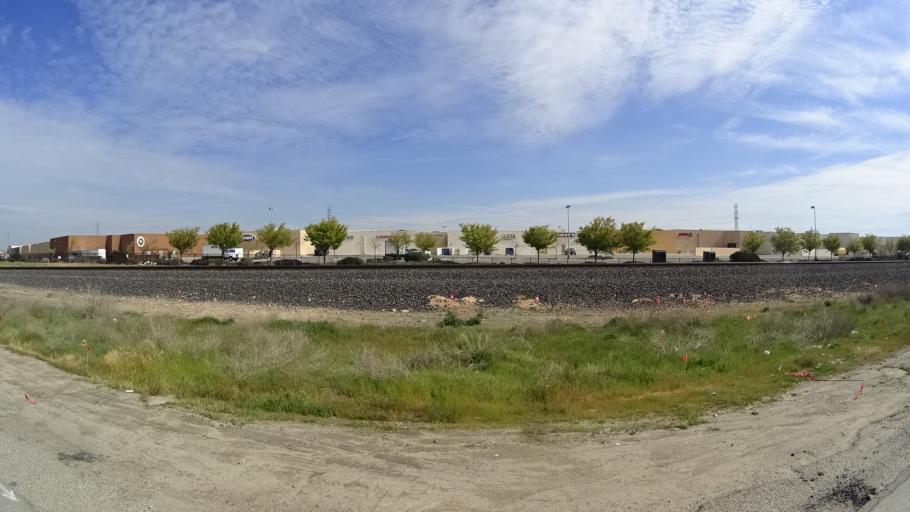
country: US
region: California
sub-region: Fresno County
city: Biola
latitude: 36.8321
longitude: -119.9126
